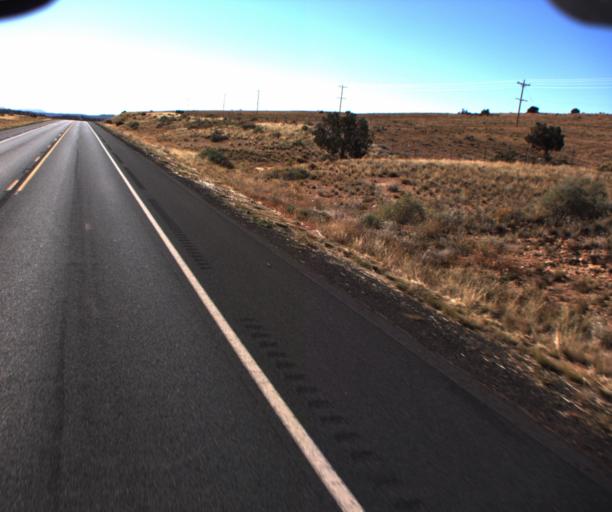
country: US
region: Arizona
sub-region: Coconino County
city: Tuba City
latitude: 36.3658
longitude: -111.5115
